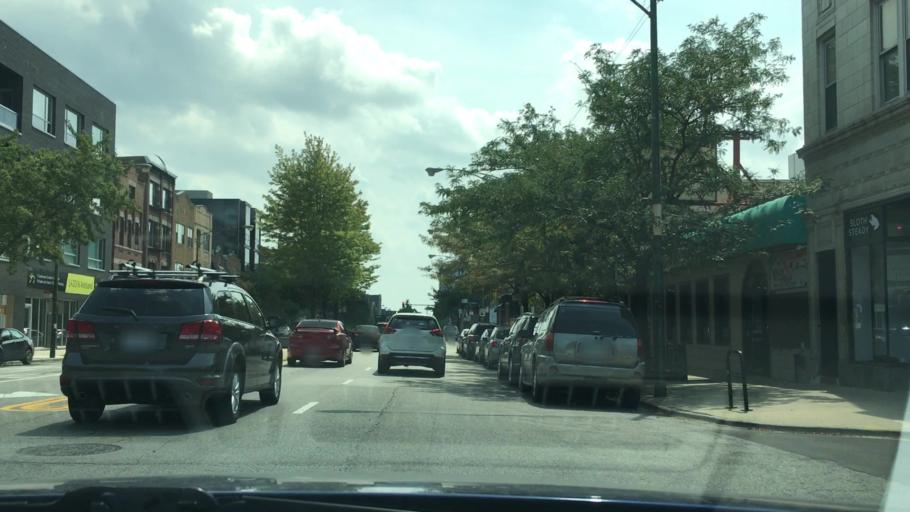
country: US
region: Illinois
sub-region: Cook County
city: Chicago
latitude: 41.9084
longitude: -87.6677
